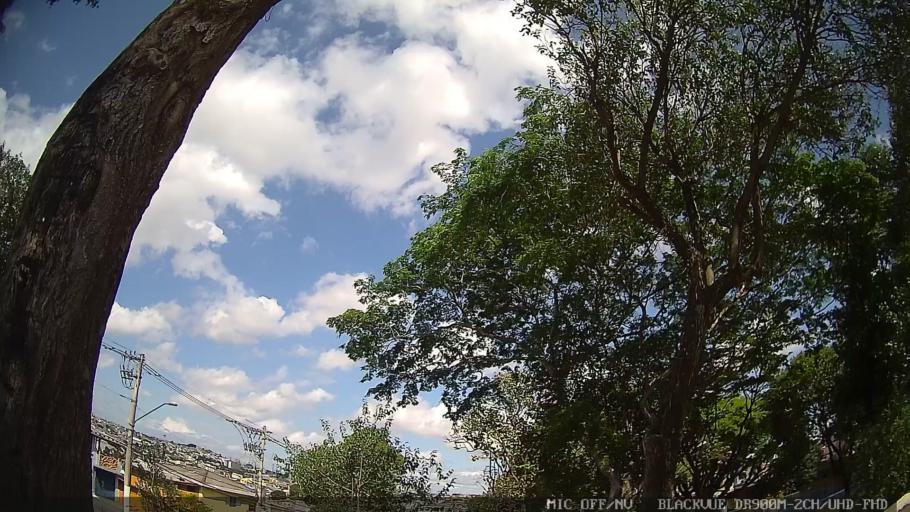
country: BR
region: Sao Paulo
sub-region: Guarulhos
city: Guarulhos
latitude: -23.4984
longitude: -46.4870
